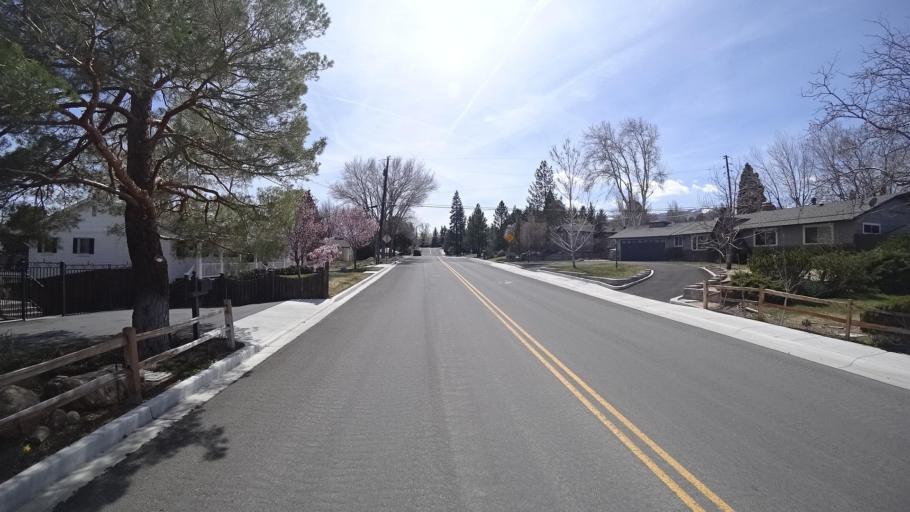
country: US
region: Nevada
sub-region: Washoe County
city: Reno
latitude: 39.4908
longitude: -119.8411
